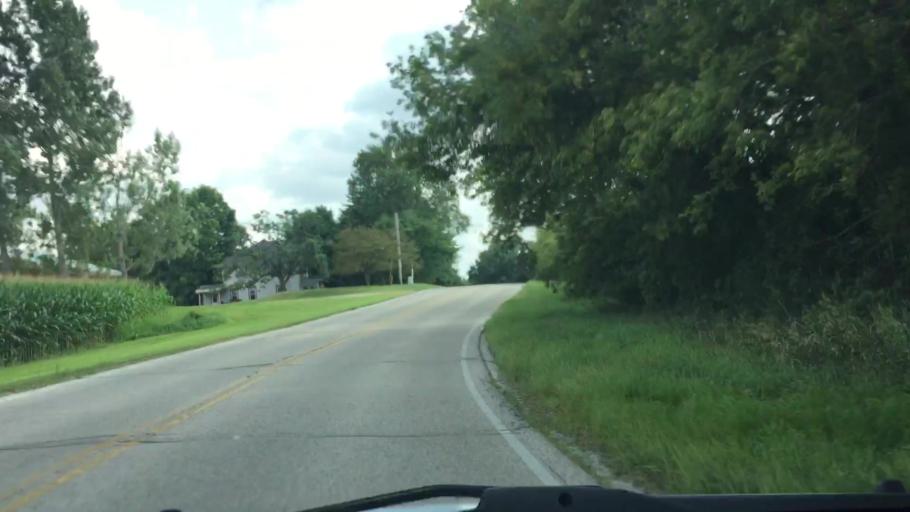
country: US
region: Wisconsin
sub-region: Waukesha County
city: Wales
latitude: 43.0266
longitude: -88.3642
